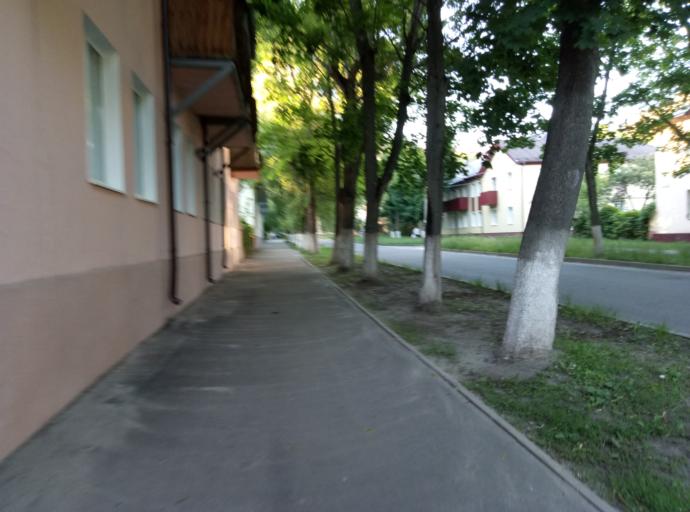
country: RU
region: Kursk
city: Kursk
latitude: 51.6731
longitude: 36.1523
